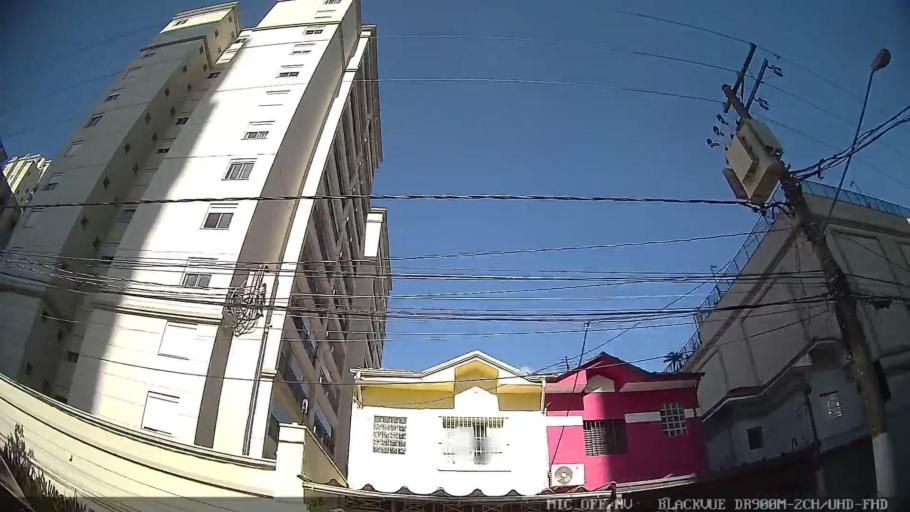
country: BR
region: Sao Paulo
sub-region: Sao Paulo
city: Sao Paulo
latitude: -23.5778
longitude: -46.6063
